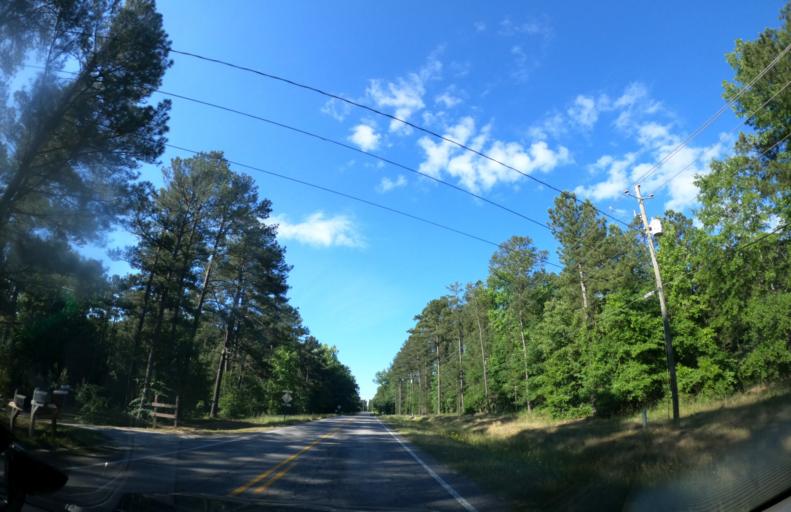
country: US
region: Georgia
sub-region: Columbia County
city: Grovetown
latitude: 33.4479
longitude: -82.2466
